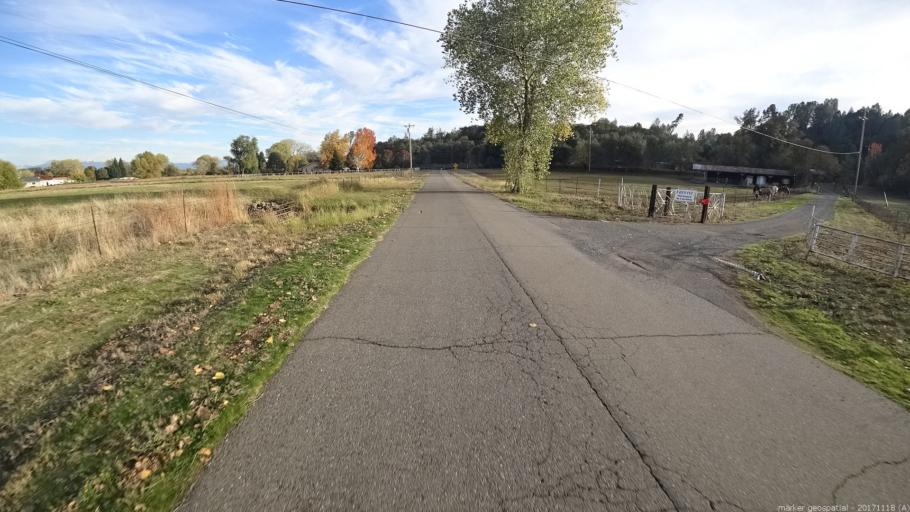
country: US
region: California
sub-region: Shasta County
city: Anderson
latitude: 40.4569
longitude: -122.3327
